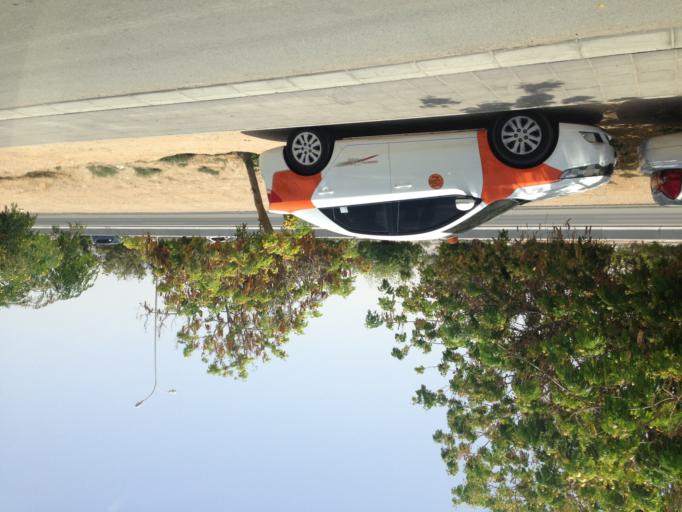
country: OM
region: Muhafazat Masqat
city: Bawshar
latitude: 23.6046
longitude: 58.3296
